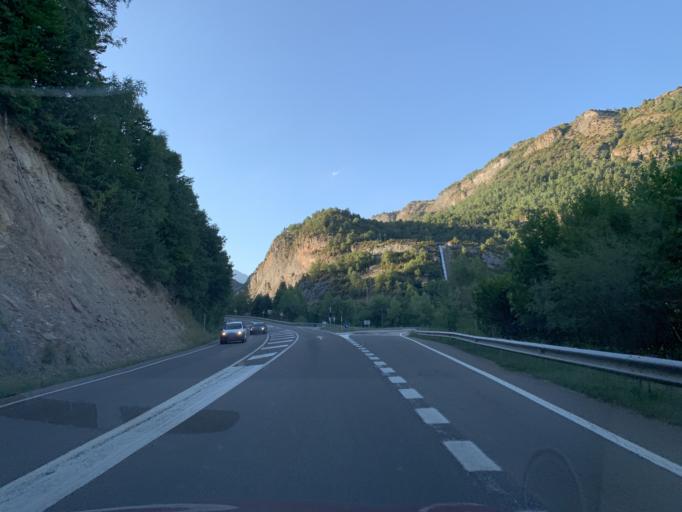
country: ES
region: Aragon
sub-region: Provincia de Huesca
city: Hoz de Jaca
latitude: 42.7262
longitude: -0.3071
